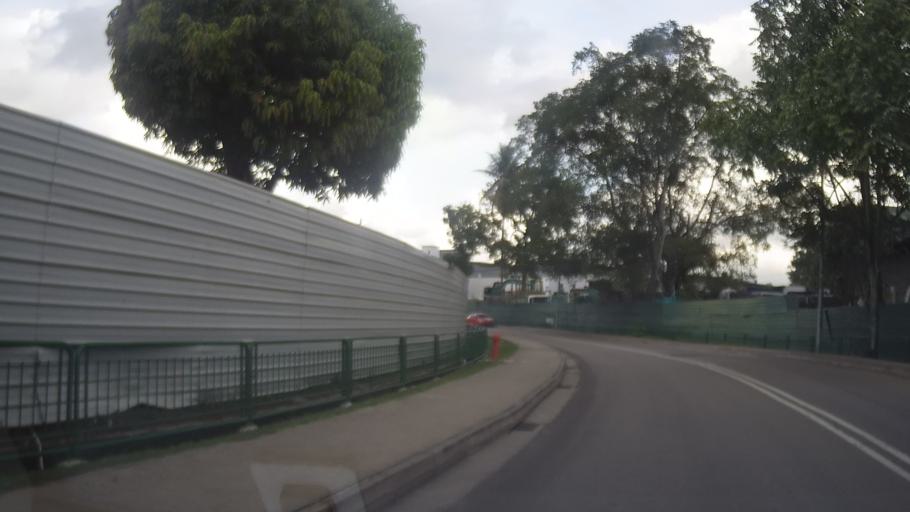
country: MY
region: Johor
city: Johor Bahru
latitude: 1.4207
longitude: 103.7450
